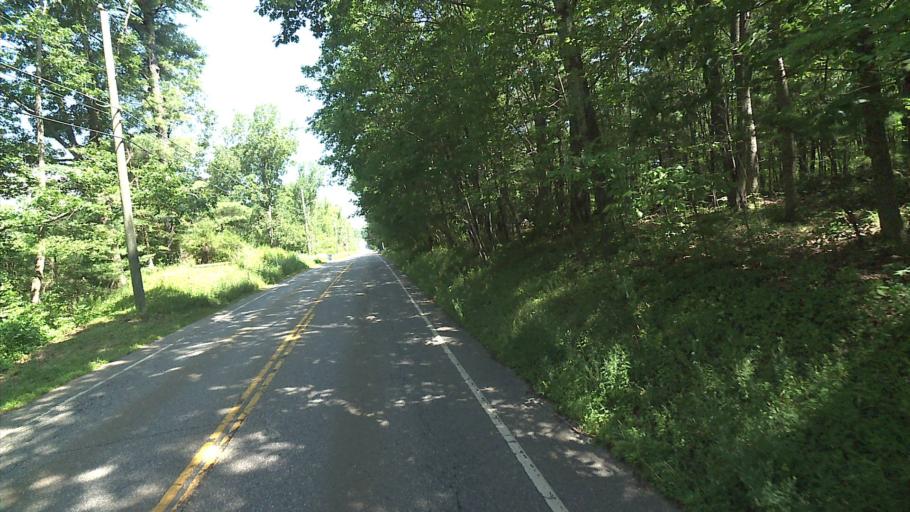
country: US
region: Connecticut
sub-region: Litchfield County
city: New Preston
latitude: 41.7564
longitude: -73.3533
